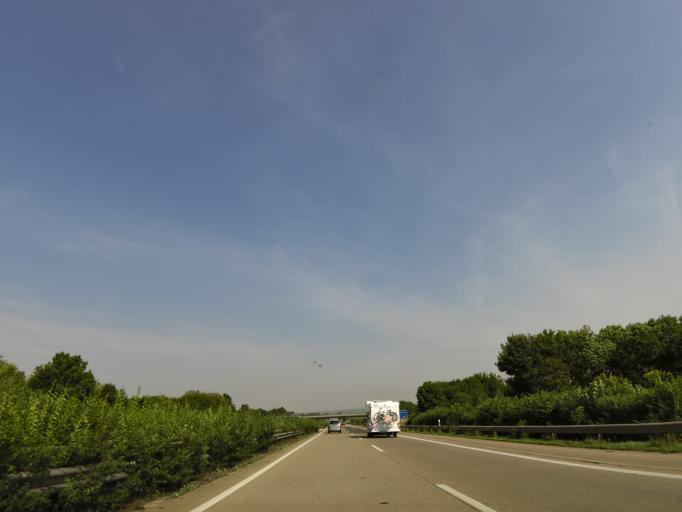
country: DE
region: Rheinland-Pfalz
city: Morstadt
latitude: 49.6651
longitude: 8.2739
